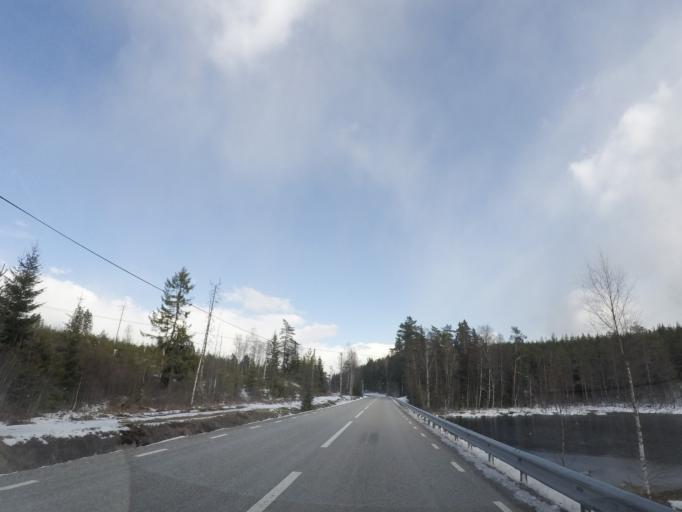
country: SE
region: OErebro
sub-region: Lindesbergs Kommun
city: Stora
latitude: 59.8944
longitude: 15.2636
